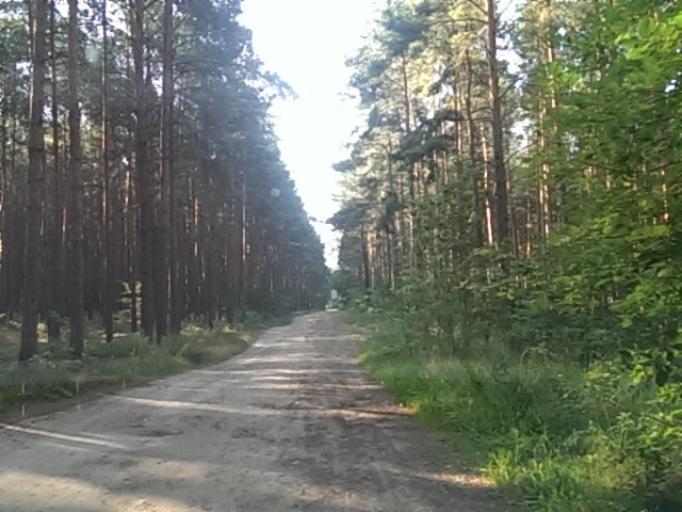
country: DE
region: Brandenburg
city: Trebbin
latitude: 52.1970
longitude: 13.1491
